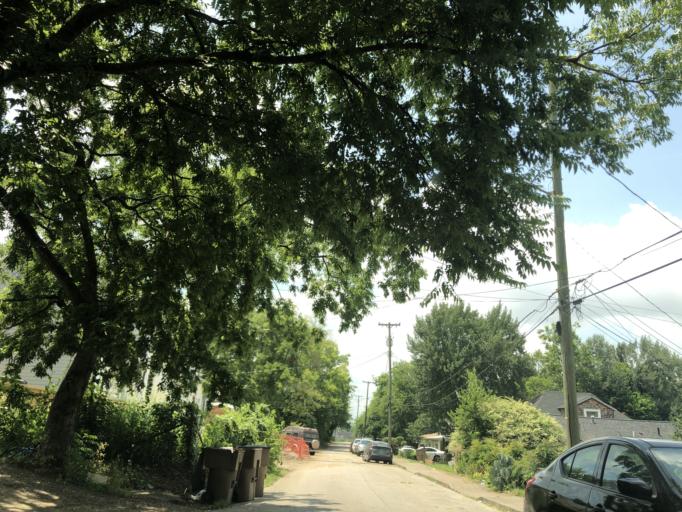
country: US
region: Tennessee
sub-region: Davidson County
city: Nashville
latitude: 36.1577
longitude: -86.8242
